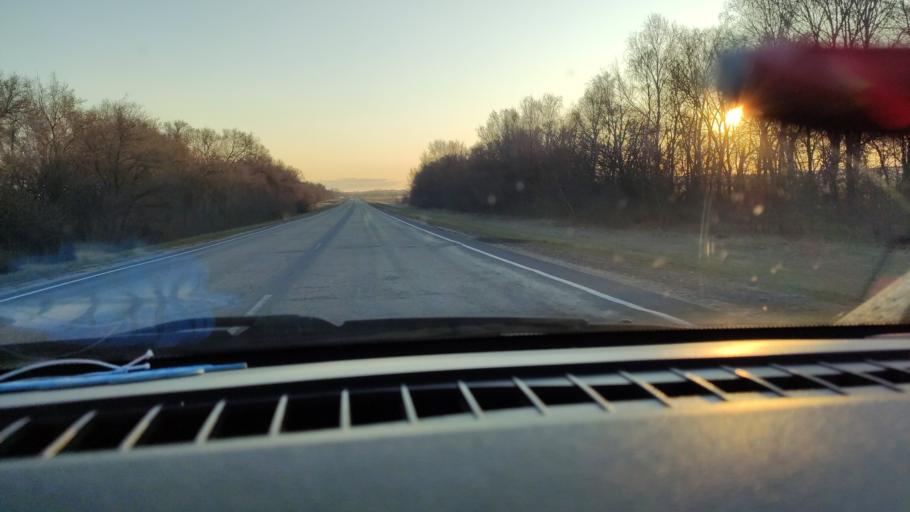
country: RU
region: Saratov
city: Sinodskoye
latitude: 51.9664
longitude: 46.6338
